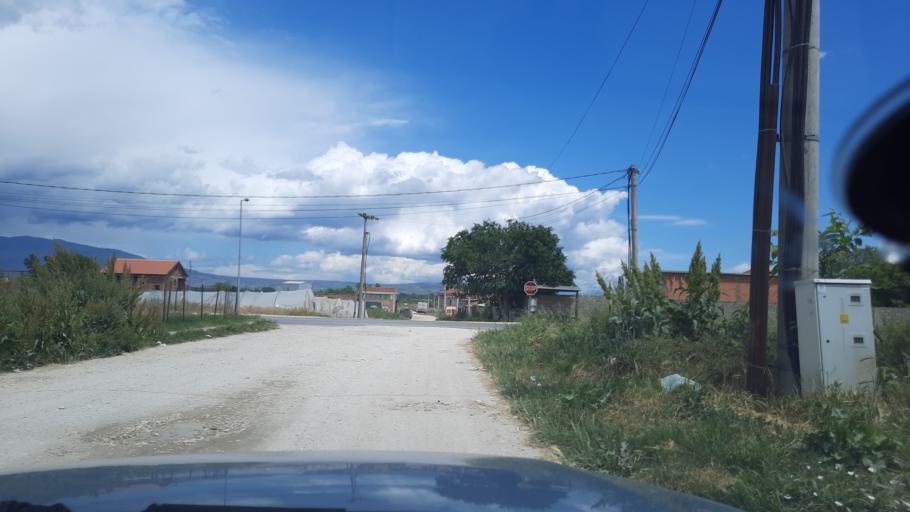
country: MK
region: Studenicani
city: Studenichani
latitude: 41.9266
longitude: 21.5405
